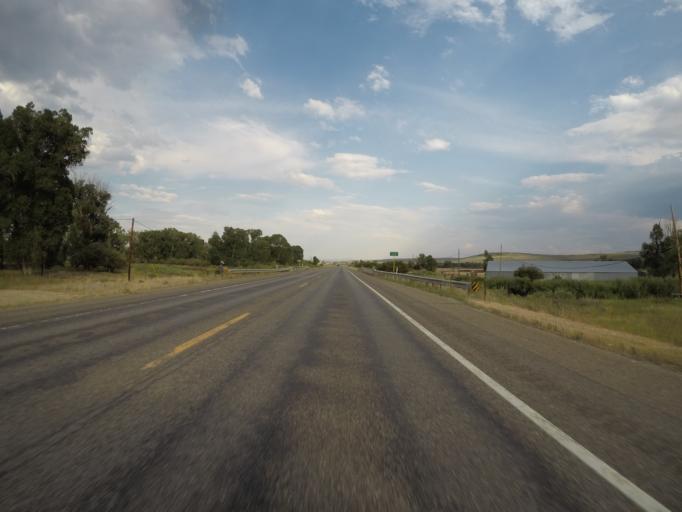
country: US
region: Colorado
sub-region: Moffat County
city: Craig
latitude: 40.5313
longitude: -107.4366
